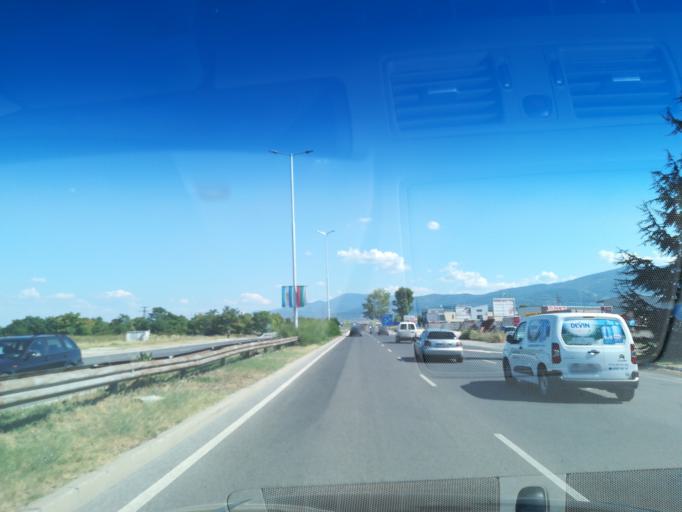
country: BG
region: Plovdiv
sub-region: Obshtina Plovdiv
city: Plovdiv
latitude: 42.1026
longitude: 24.7859
